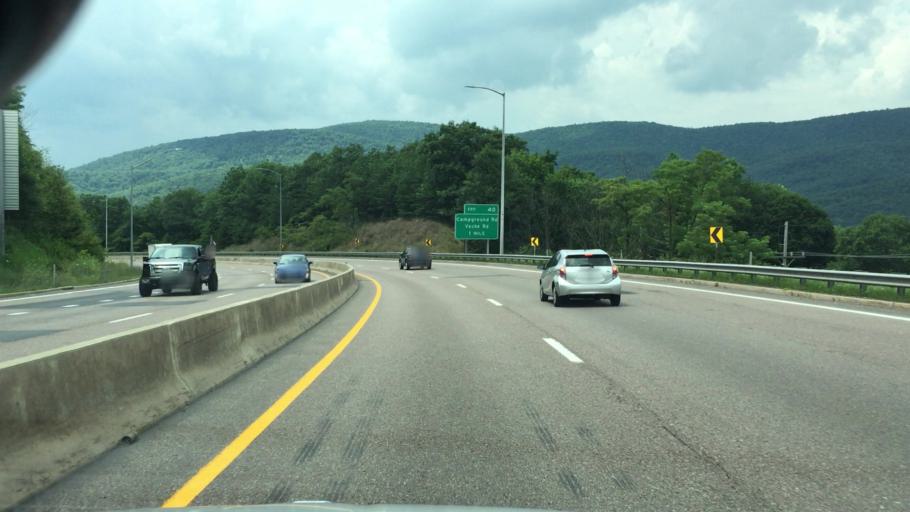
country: US
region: Maryland
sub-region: Allegany County
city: La Vale
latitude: 39.6414
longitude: -78.8130
